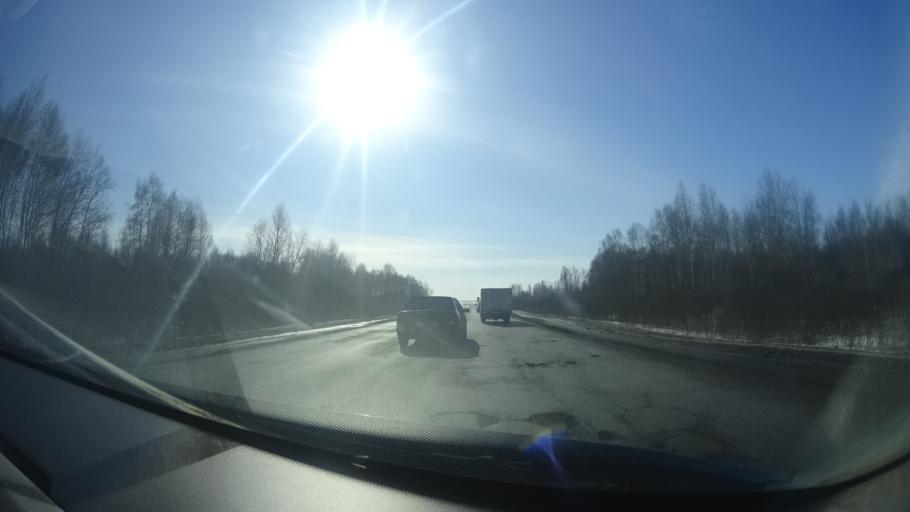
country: RU
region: Bashkortostan
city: Mikhaylovka
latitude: 54.9024
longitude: 55.7273
